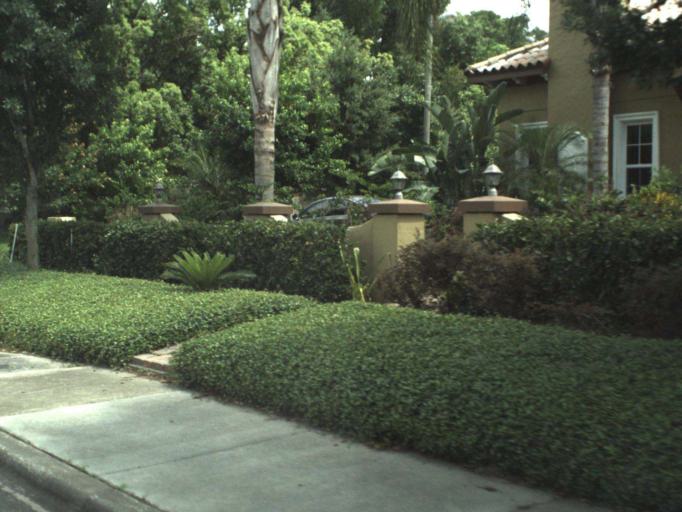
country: US
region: Florida
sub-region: Orange County
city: Winter Park
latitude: 28.6004
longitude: -81.3299
